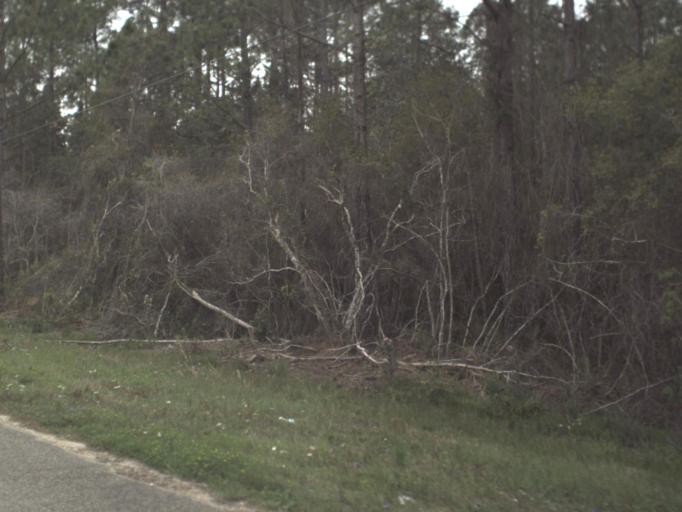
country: US
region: Florida
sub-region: Gulf County
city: Port Saint Joe
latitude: 29.8450
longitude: -85.2640
